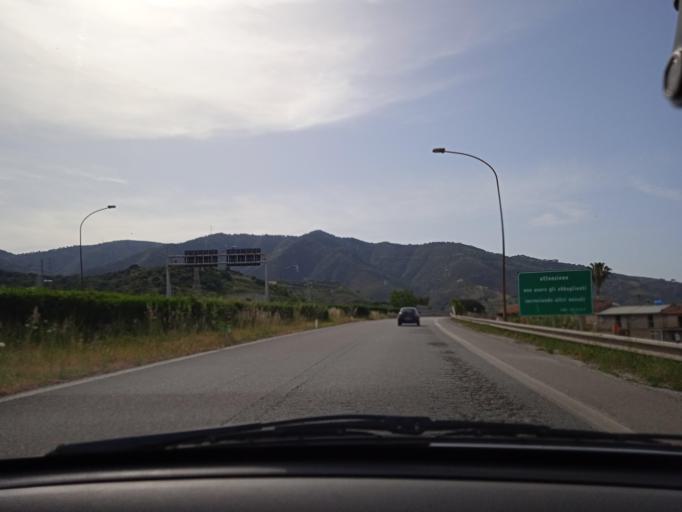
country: IT
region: Sicily
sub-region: Messina
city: Falcone
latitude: 38.1140
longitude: 15.0683
